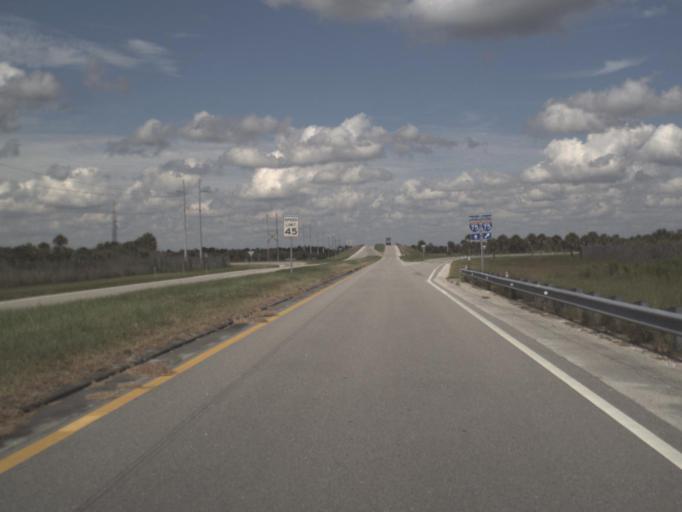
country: US
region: Florida
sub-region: Collier County
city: Immokalee
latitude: 26.1487
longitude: -81.3450
